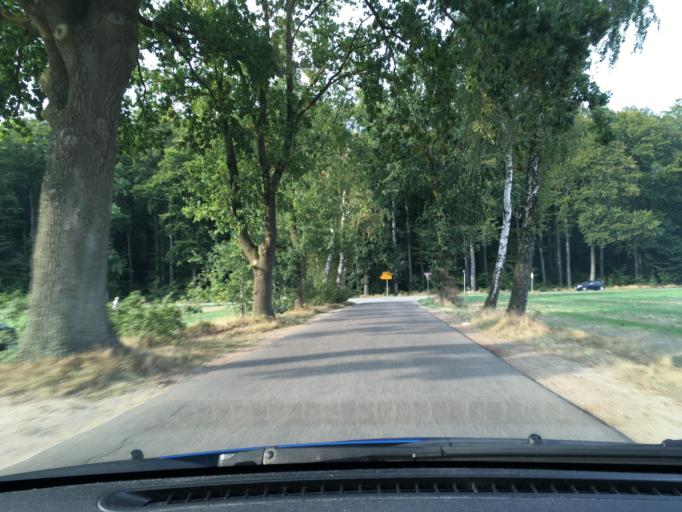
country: DE
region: Lower Saxony
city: Toppenstedt
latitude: 53.3123
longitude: 10.0947
